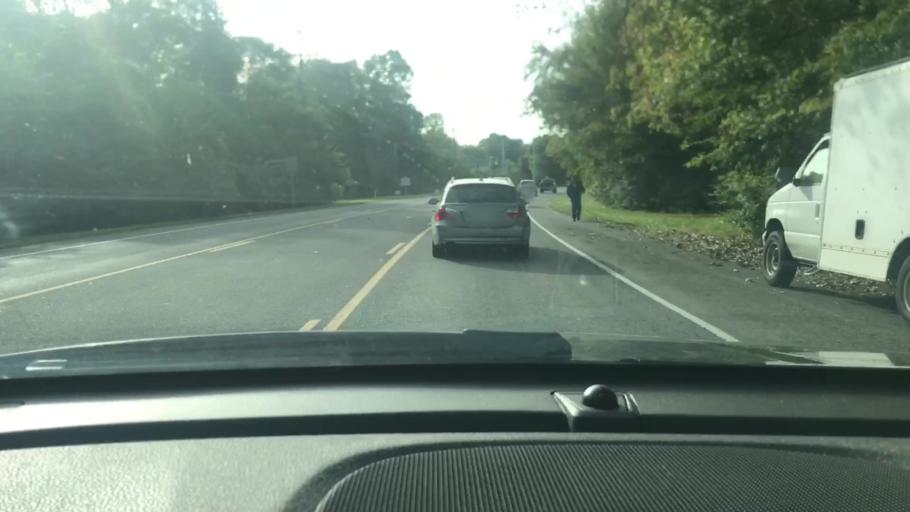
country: US
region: Tennessee
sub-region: Williamson County
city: Franklin
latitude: 35.9239
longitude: -86.8771
